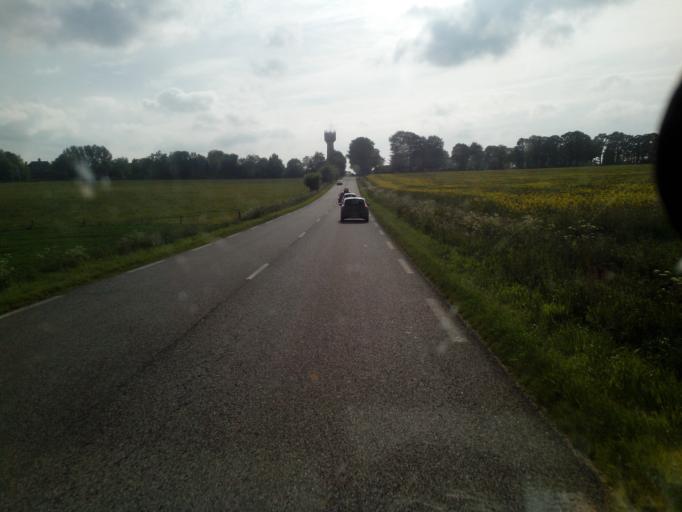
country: FR
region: Haute-Normandie
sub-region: Departement de la Seine-Maritime
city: Yerville
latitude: 49.6699
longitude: 0.9258
